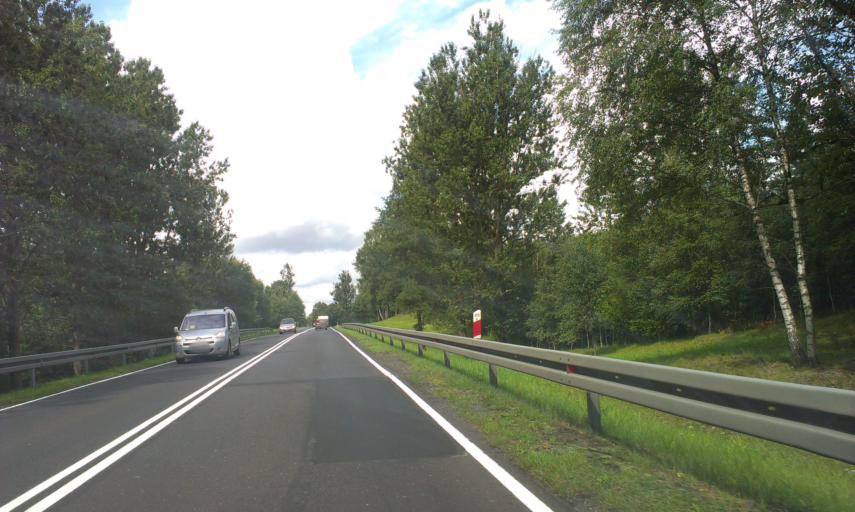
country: PL
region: West Pomeranian Voivodeship
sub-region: Powiat koszalinski
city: Bobolice
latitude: 53.9675
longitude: 16.5677
